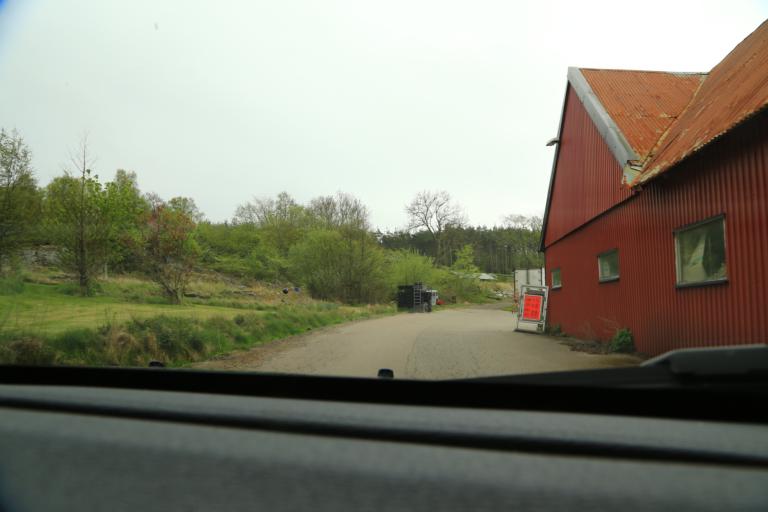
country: SE
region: Halland
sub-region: Kungsbacka Kommun
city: Frillesas
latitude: 57.2252
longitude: 12.1537
